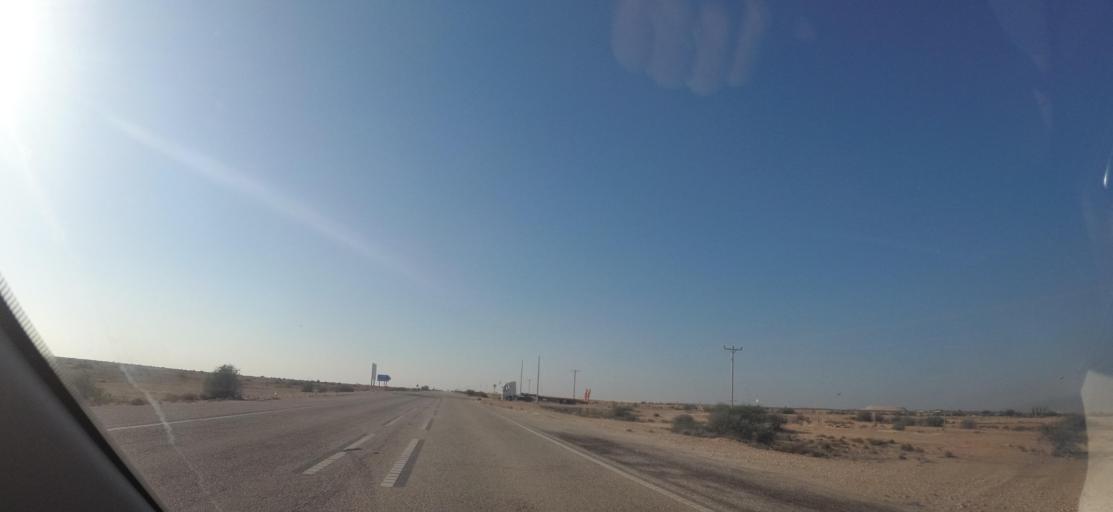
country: QA
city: Al Ghuwayriyah
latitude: 25.8581
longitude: 51.2486
